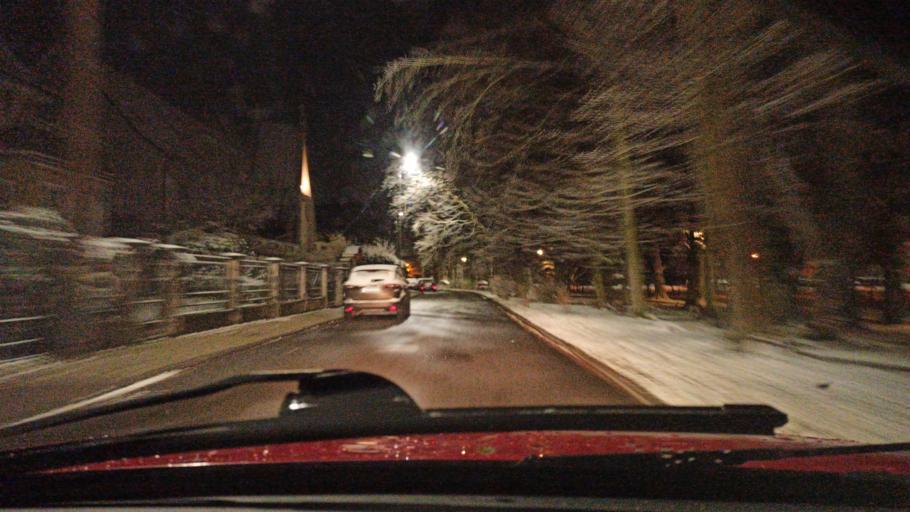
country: PL
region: Warmian-Masurian Voivodeship
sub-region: Powiat elblaski
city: Elblag
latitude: 54.1746
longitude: 19.4089
